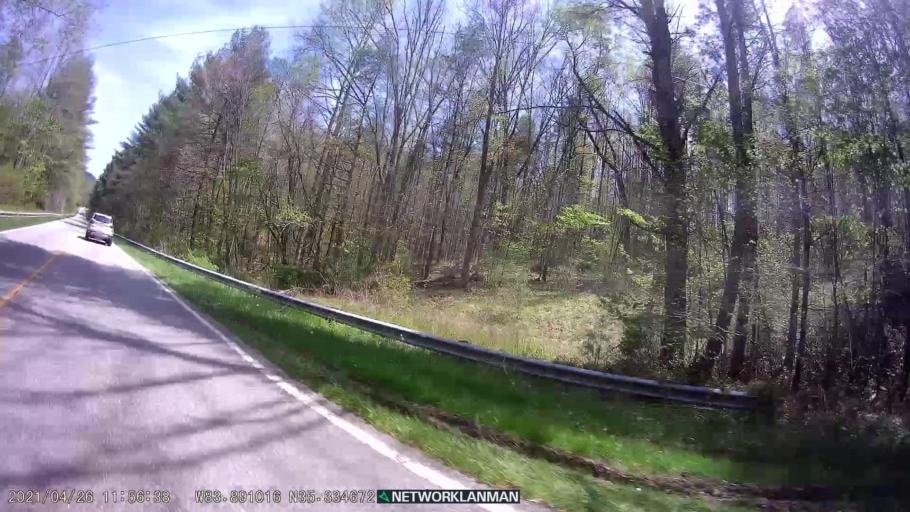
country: US
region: North Carolina
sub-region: Graham County
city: Robbinsville
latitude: 35.3346
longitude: -83.8908
